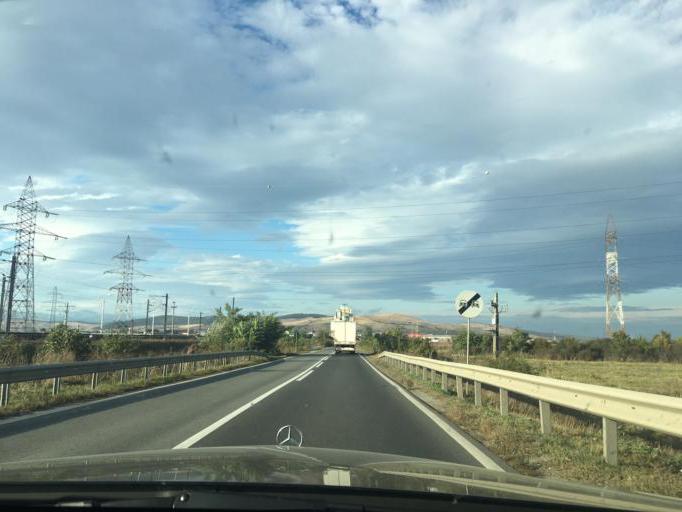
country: RO
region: Alba
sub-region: Municipiul Alba Iulia
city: Alba Iulia
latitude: 46.0792
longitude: 23.5965
